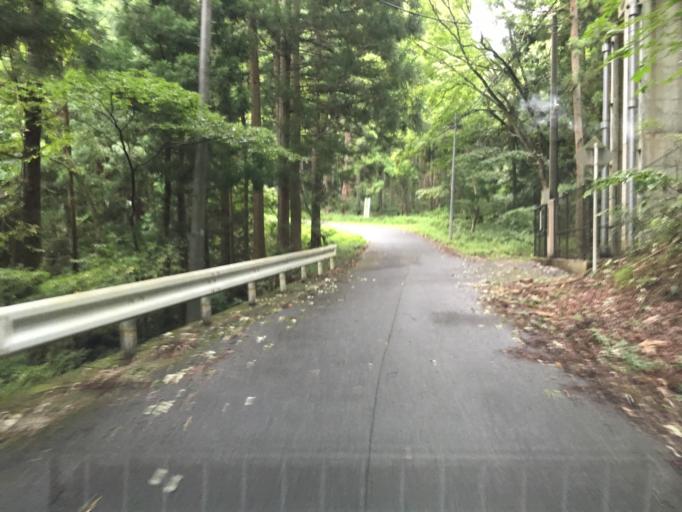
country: JP
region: Fukushima
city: Fukushima-shi
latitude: 37.7976
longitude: 140.3792
